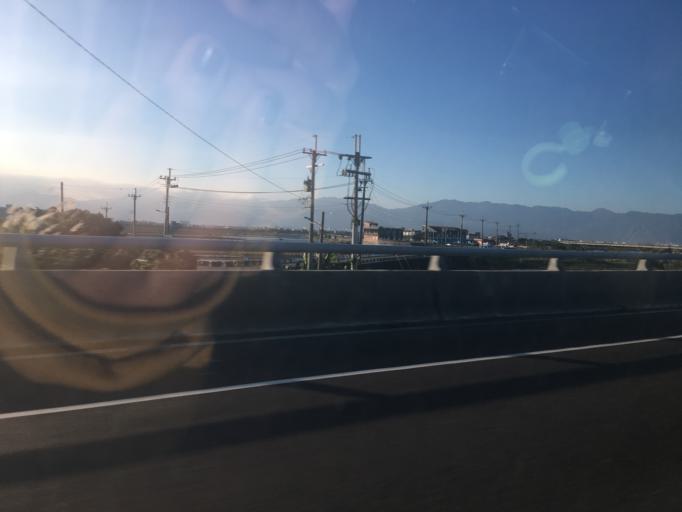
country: TW
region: Taiwan
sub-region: Yilan
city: Yilan
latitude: 24.7167
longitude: 121.8205
